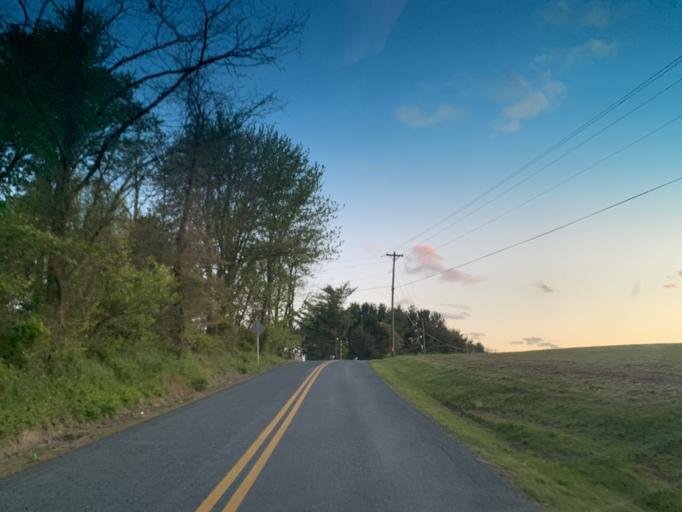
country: US
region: Pennsylvania
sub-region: York County
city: Susquehanna Trails
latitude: 39.6798
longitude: -76.3406
